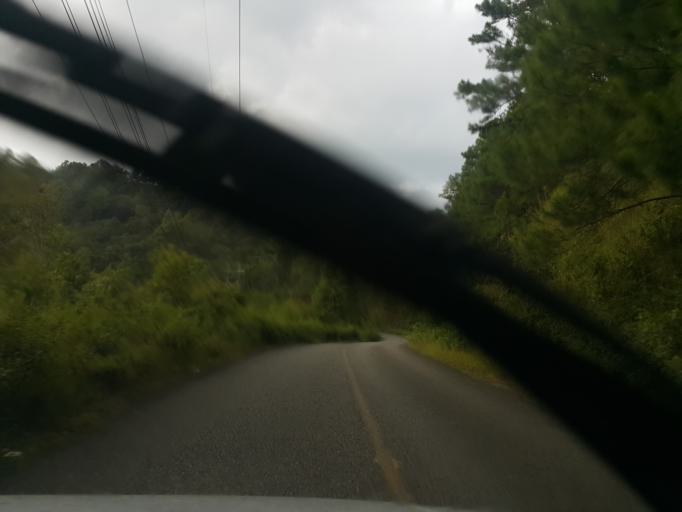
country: TH
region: Mae Hong Son
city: Khun Yuam
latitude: 18.7690
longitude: 98.1689
